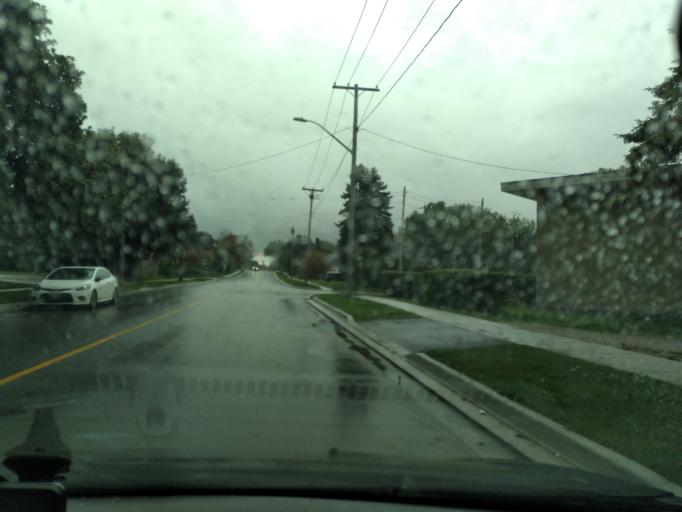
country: CA
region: Ontario
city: Barrie
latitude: 44.4014
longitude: -79.6754
